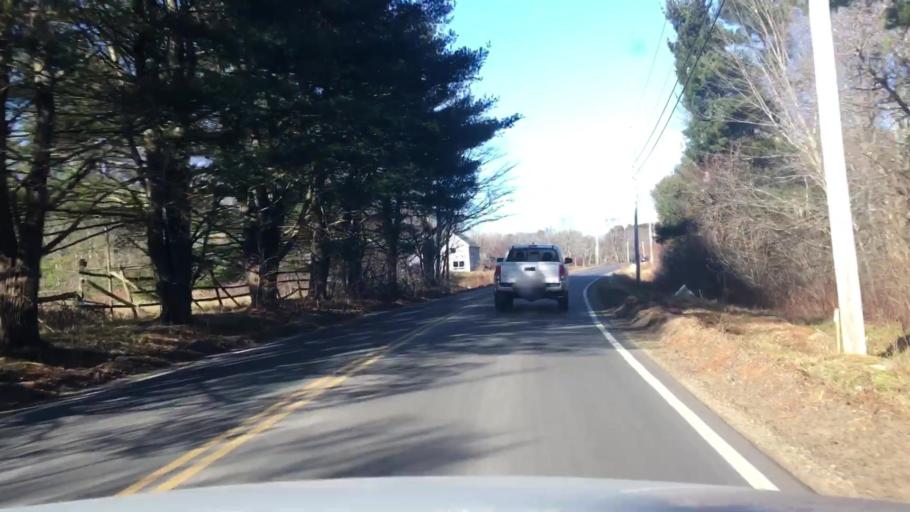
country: US
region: Maine
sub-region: York County
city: Arundel
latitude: 43.4084
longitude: -70.4929
